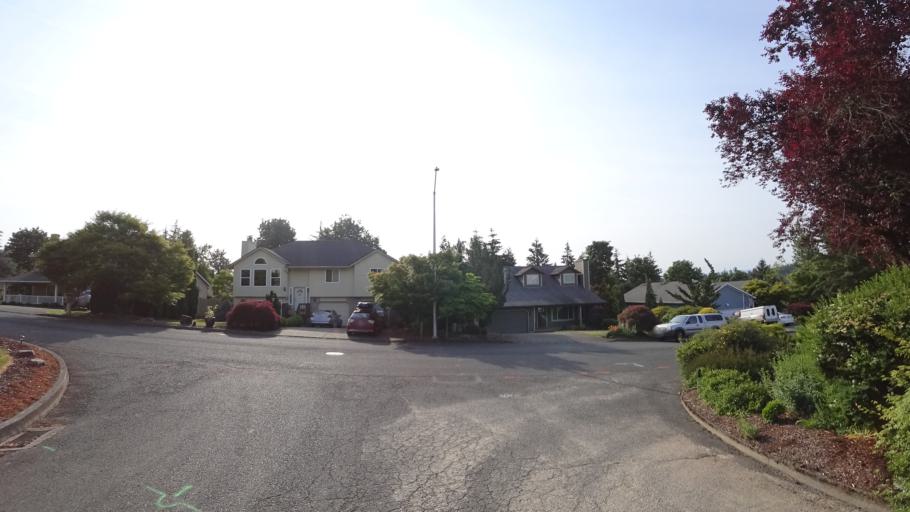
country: US
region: Oregon
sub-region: Clackamas County
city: Happy Valley
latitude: 45.4631
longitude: -122.5153
